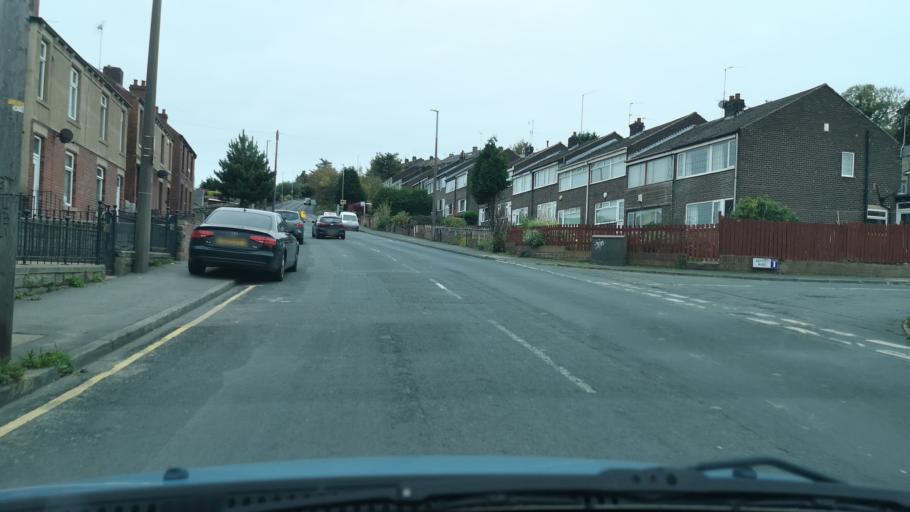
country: GB
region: England
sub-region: Kirklees
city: Dewsbury
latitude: 53.6721
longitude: -1.6272
